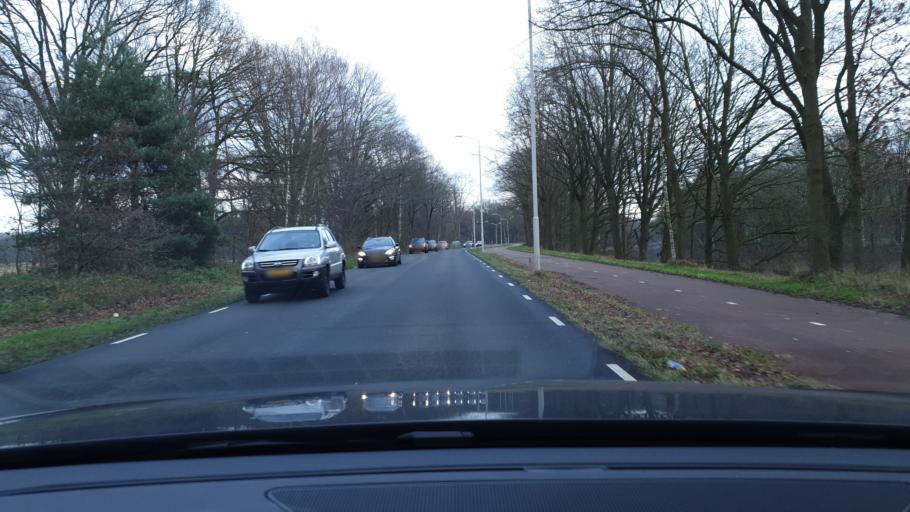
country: NL
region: North Brabant
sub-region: Gemeente Best
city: Best
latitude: 51.5027
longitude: 5.4218
